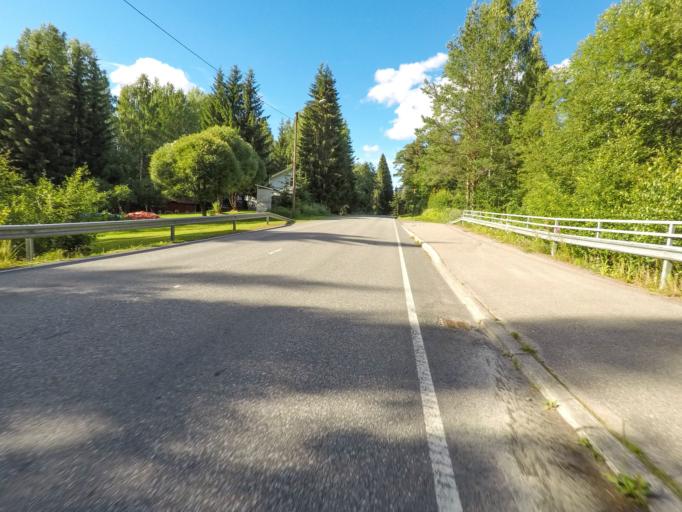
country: FI
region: South Karelia
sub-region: Imatra
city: Imatra
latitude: 61.1489
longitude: 28.7531
